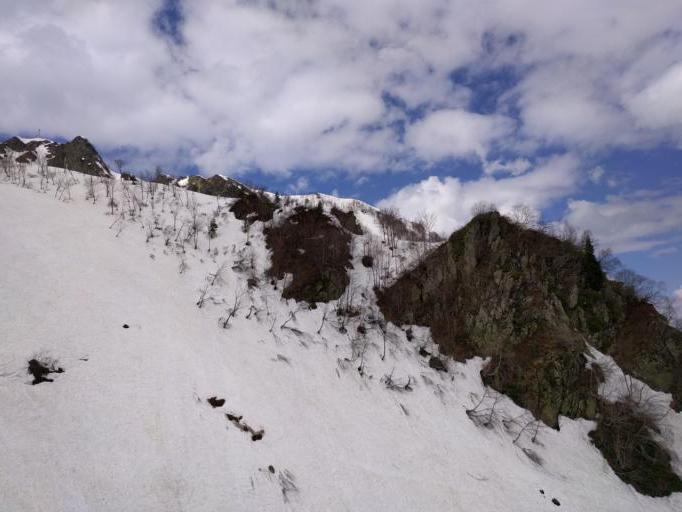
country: RU
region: Krasnodarskiy
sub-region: Sochi City
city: Krasnaya Polyana
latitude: 43.6337
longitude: 40.3122
